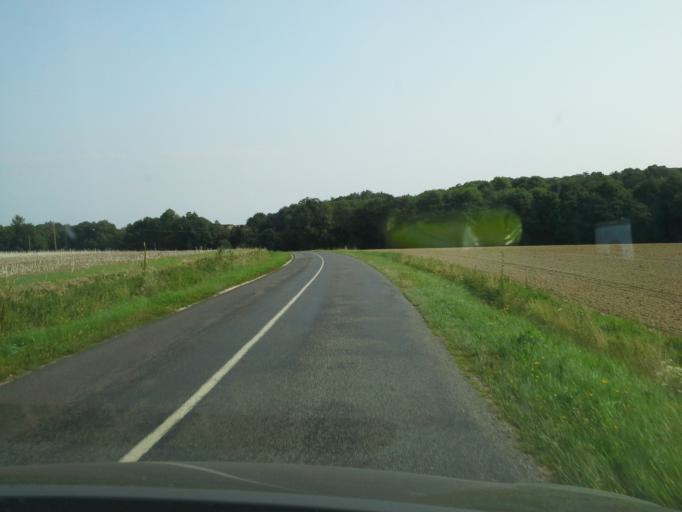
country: FR
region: Centre
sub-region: Departement du Loir-et-Cher
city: La Ville-aux-Clercs
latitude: 47.9048
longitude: 1.0443
